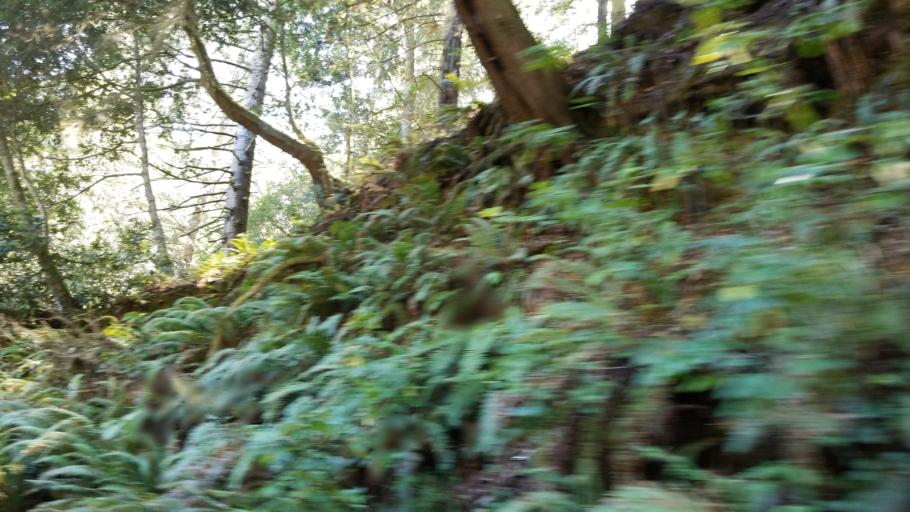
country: US
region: California
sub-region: Mendocino County
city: Fort Bragg
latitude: 39.4486
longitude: -123.7796
